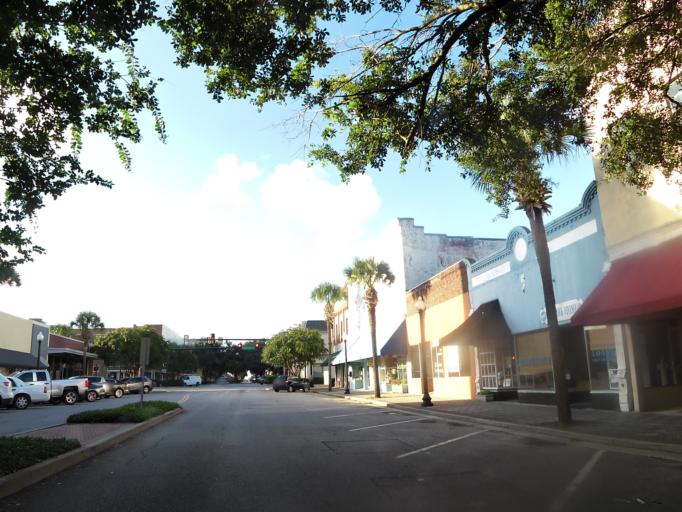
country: US
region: Georgia
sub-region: Glynn County
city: Brunswick
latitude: 31.1484
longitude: -81.4951
